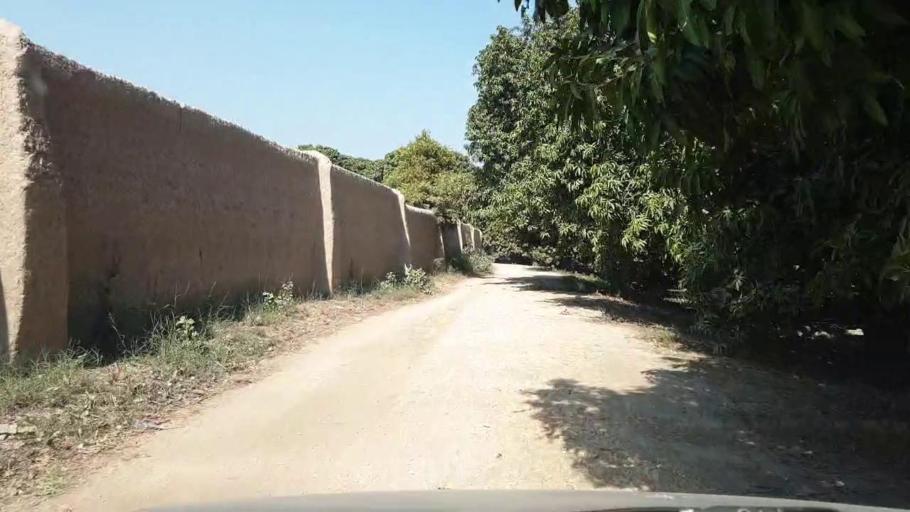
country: PK
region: Sindh
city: Tando Jam
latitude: 25.4027
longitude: 68.6310
